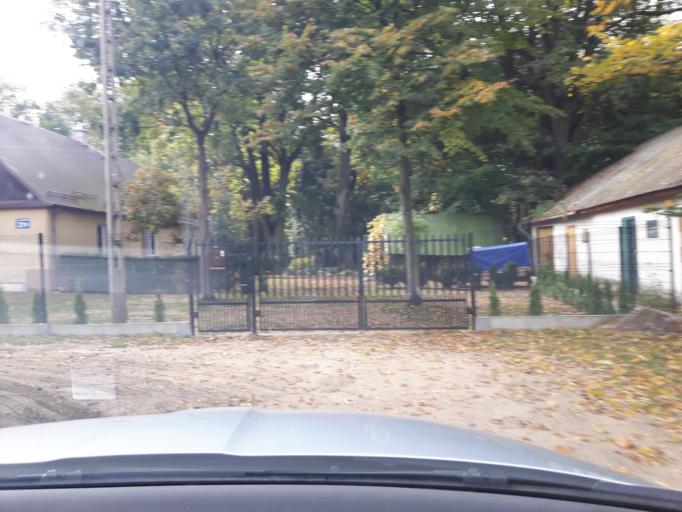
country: PL
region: Masovian Voivodeship
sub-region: Powiat wolominski
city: Zabki
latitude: 52.2988
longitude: 21.1234
